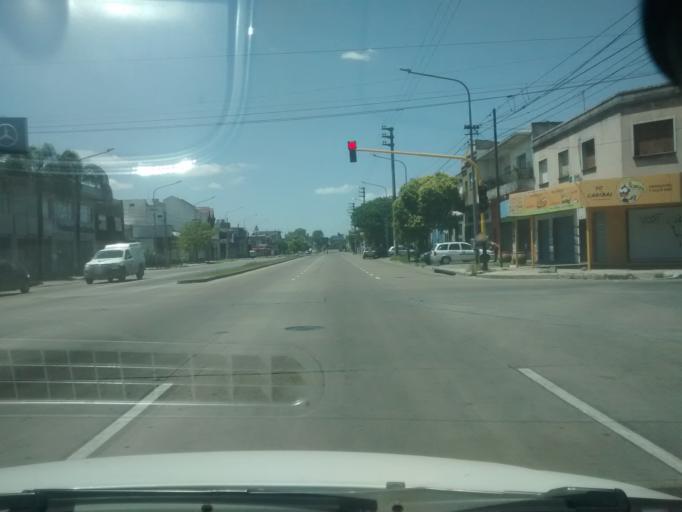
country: AR
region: Buenos Aires
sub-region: Partido de Moron
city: Moron
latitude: -34.6605
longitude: -58.6144
